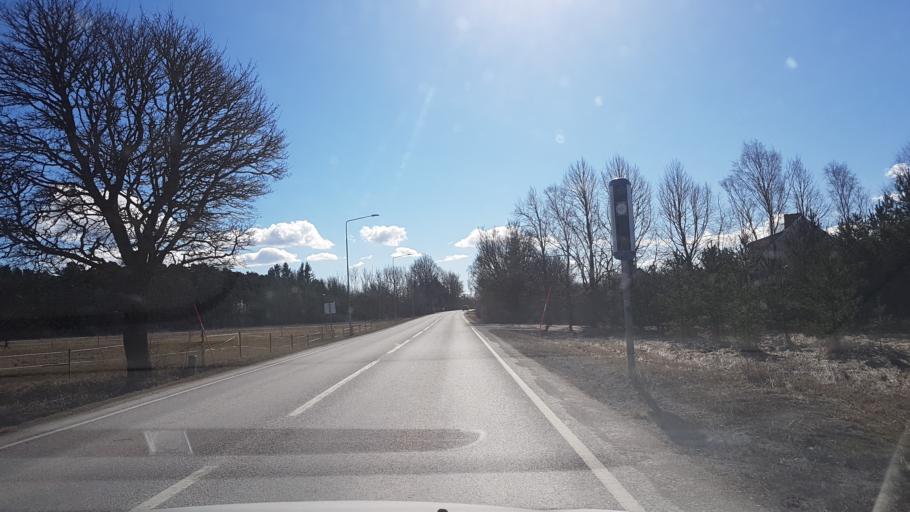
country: SE
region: Gotland
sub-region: Gotland
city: Visby
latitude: 57.5218
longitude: 18.4421
